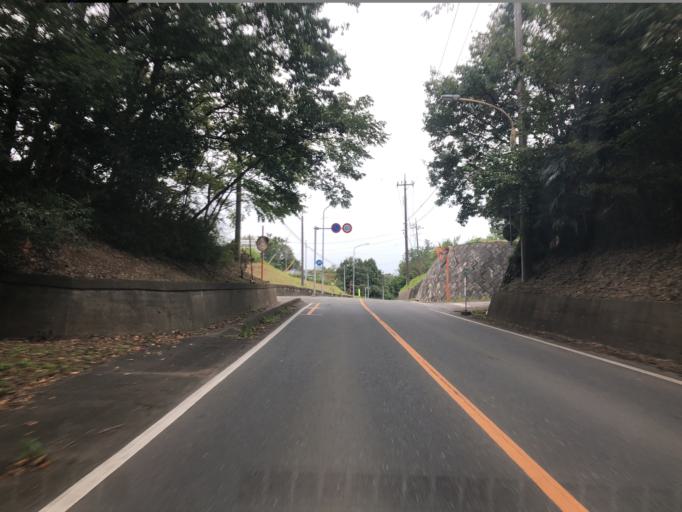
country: JP
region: Saitama
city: Fukiage-fujimi
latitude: 36.0690
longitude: 139.3947
